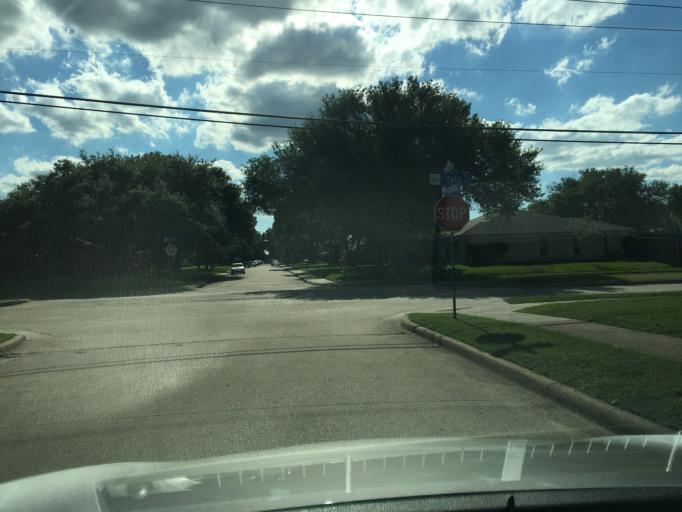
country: US
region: Texas
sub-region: Dallas County
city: Richardson
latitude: 32.9467
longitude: -96.6910
